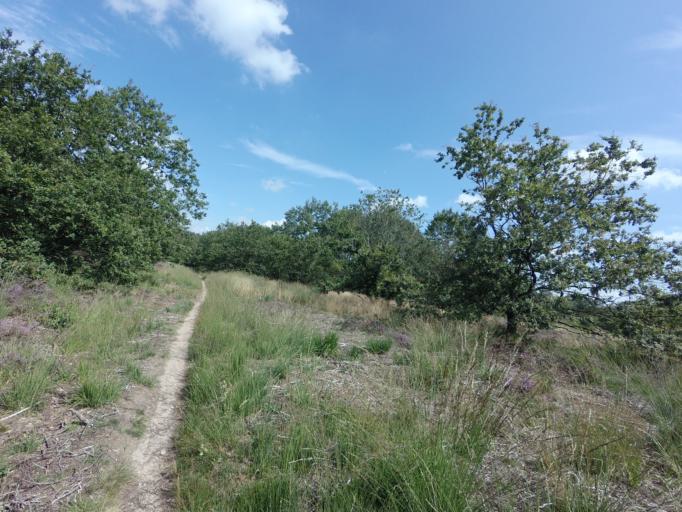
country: NL
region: Gelderland
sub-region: Gemeente Ede
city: Ede
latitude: 52.0511
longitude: 5.6977
